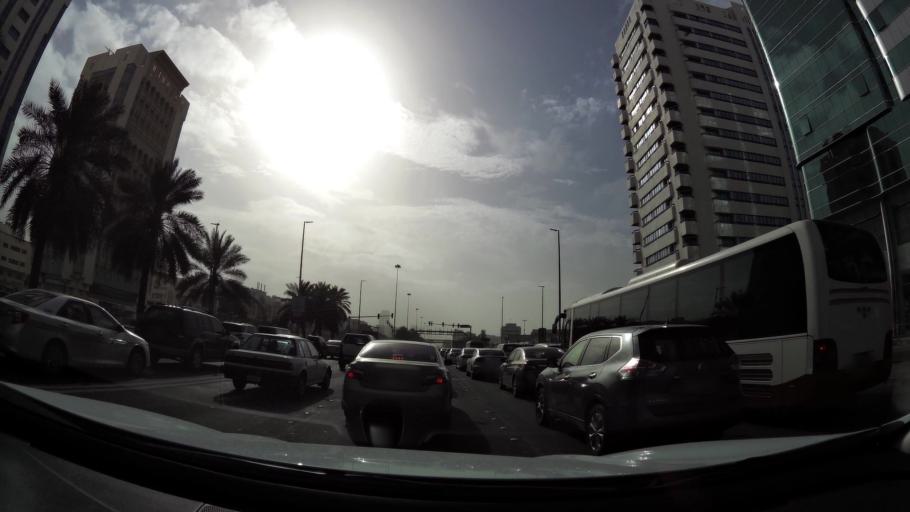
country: AE
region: Abu Dhabi
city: Abu Dhabi
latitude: 24.4741
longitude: 54.3744
